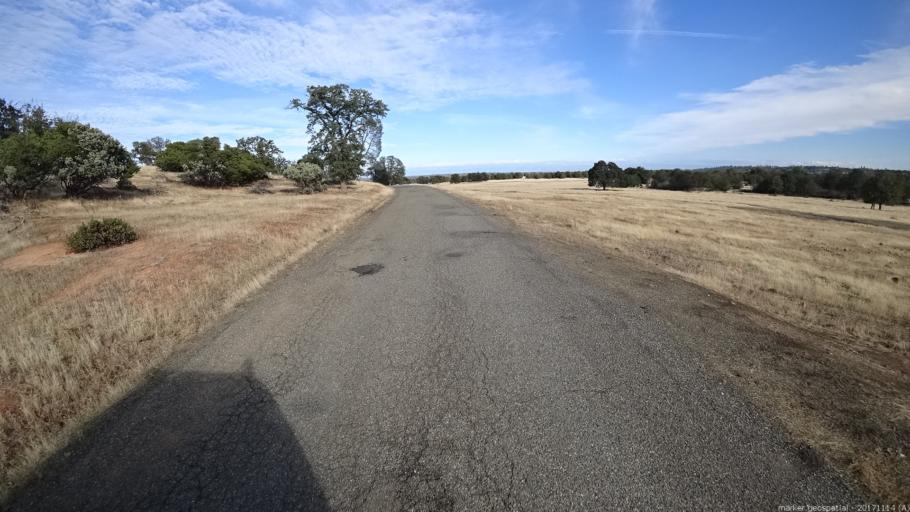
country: US
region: California
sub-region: Shasta County
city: Shasta
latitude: 40.3837
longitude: -122.5581
